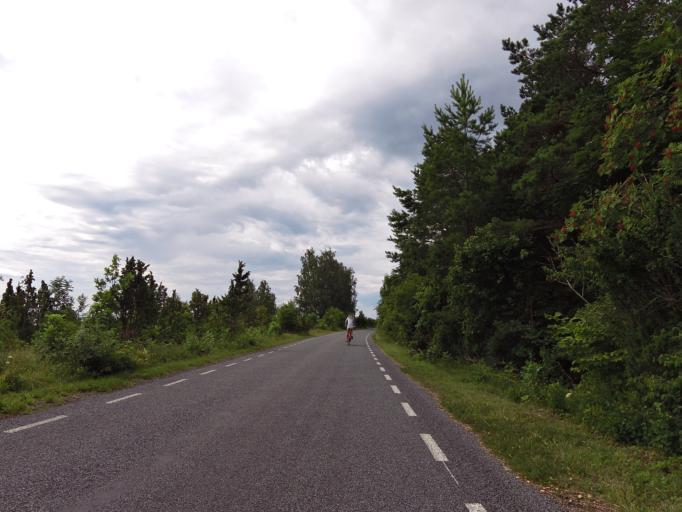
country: EE
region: Hiiumaa
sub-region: Kaerdla linn
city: Kardla
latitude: 58.7818
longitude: 22.8267
